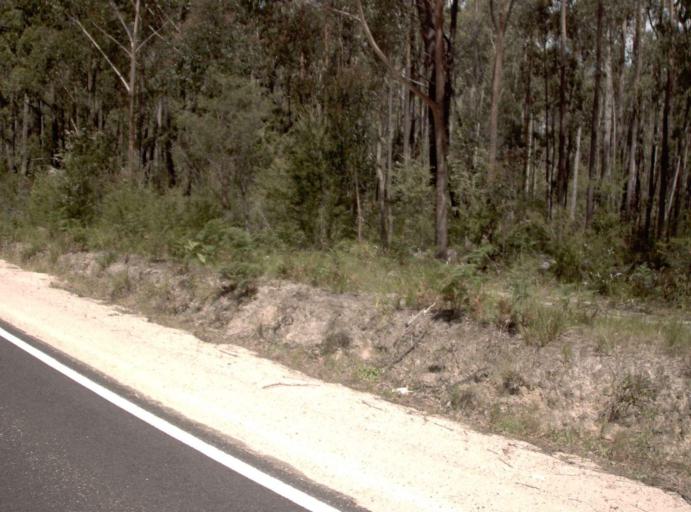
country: AU
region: New South Wales
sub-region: Bombala
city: Bombala
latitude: -37.5670
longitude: 149.1886
